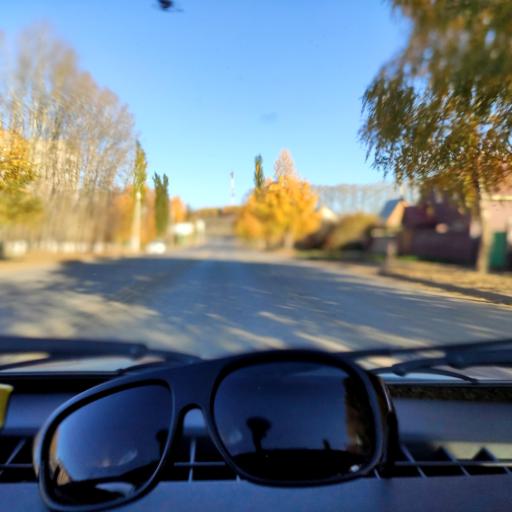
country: RU
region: Bashkortostan
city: Blagoveshchensk
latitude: 55.0530
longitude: 55.9512
